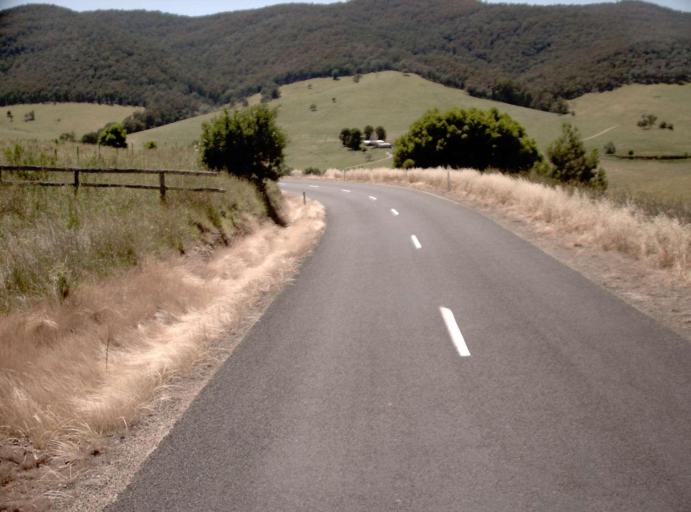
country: AU
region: Victoria
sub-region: East Gippsland
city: Lakes Entrance
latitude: -37.4165
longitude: 148.2048
